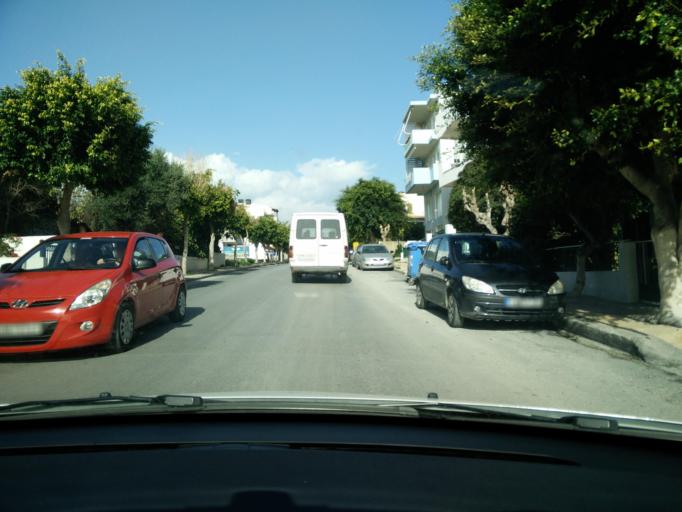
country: GR
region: Crete
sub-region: Nomos Lasithiou
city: Ierapetra
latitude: 35.0110
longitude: 25.7359
